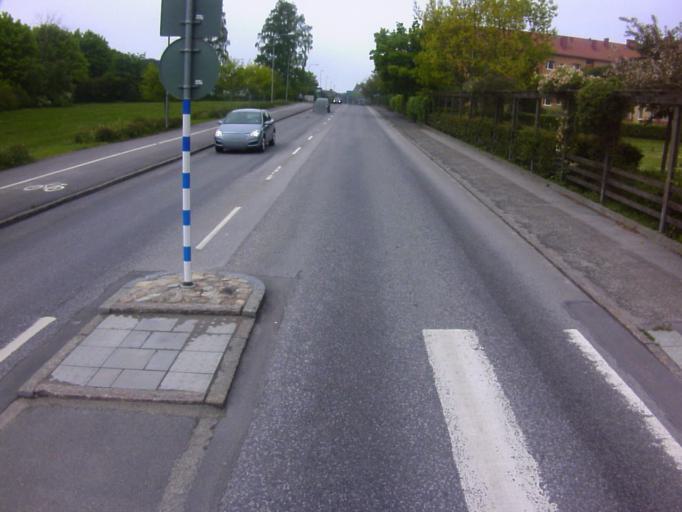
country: SE
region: Blekinge
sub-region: Solvesborgs Kommun
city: Soelvesborg
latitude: 56.0575
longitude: 14.5888
